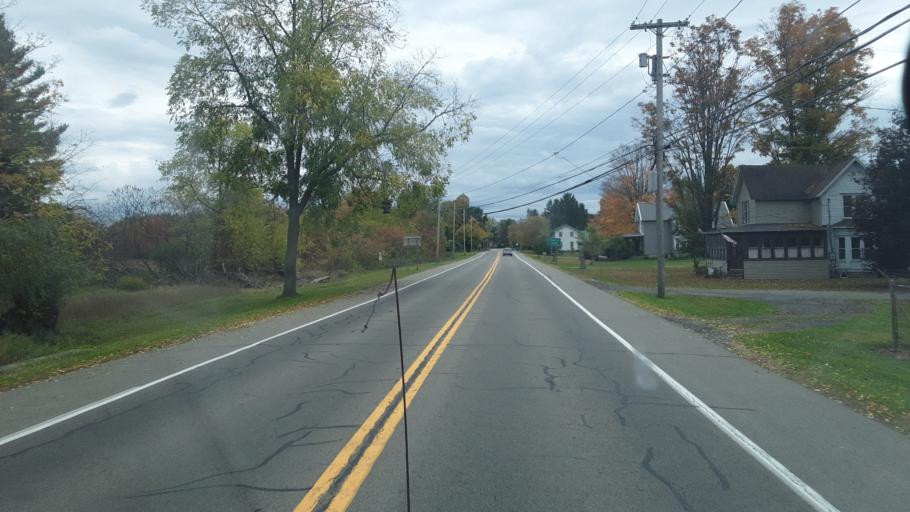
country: US
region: New York
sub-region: Allegany County
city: Belmont
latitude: 42.2182
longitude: -78.0227
